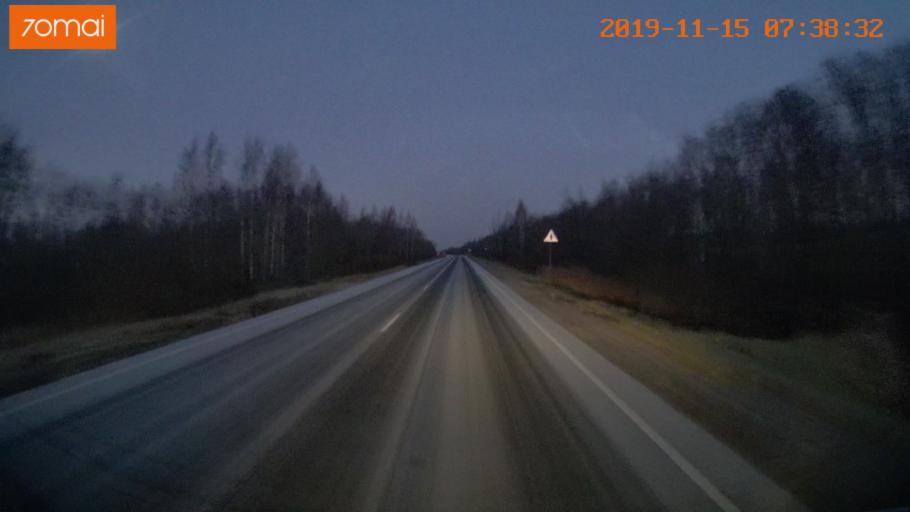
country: RU
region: Vologda
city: Sheksna
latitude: 58.7582
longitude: 38.3998
